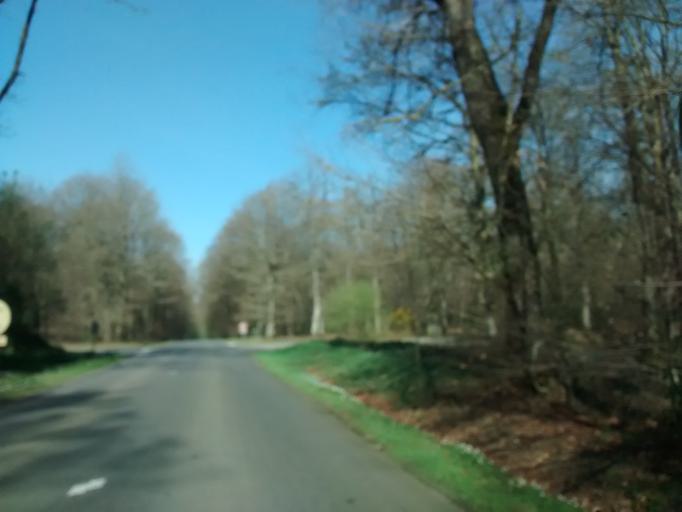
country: FR
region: Brittany
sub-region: Departement d'Ille-et-Vilaine
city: Saint-Sulpice-la-Foret
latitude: 48.2074
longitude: -1.5446
